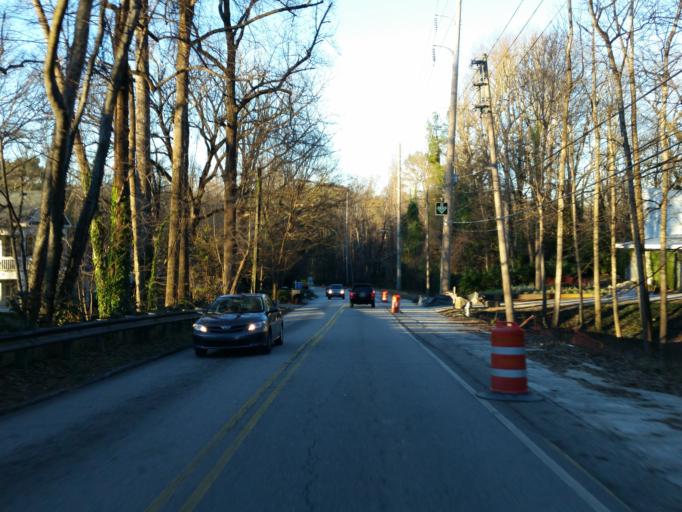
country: US
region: Georgia
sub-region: Cobb County
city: Vinings
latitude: 33.8356
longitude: -84.4075
